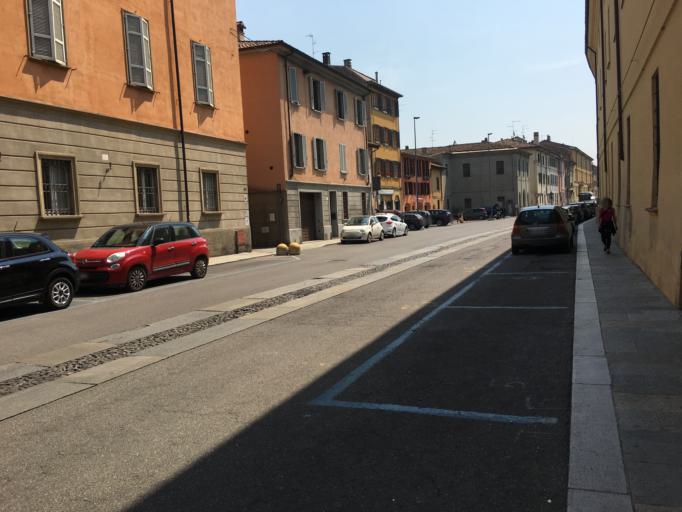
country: IT
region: Emilia-Romagna
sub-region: Provincia di Piacenza
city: Piacenza
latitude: 45.0566
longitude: 9.6818
